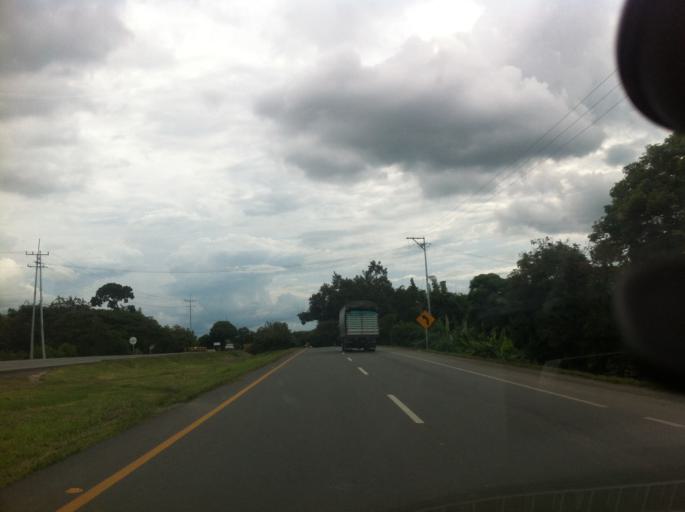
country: CO
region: Valle del Cauca
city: El Cerrito
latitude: 3.7087
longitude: -76.3196
